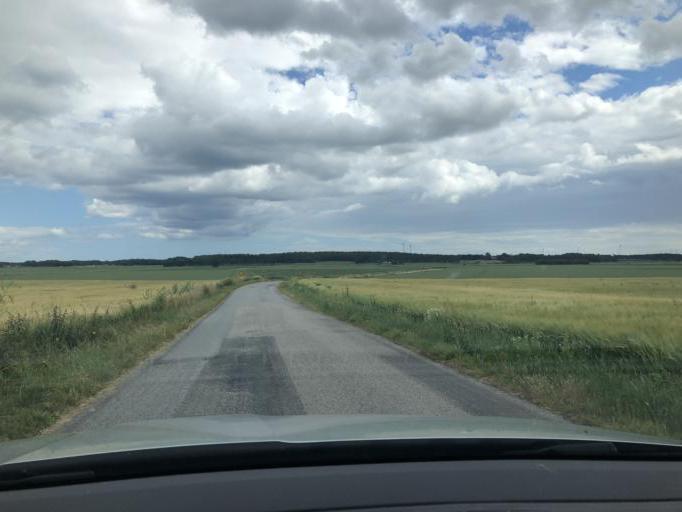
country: SE
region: Blekinge
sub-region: Solvesborgs Kommun
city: Soelvesborg
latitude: 56.1007
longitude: 14.6227
